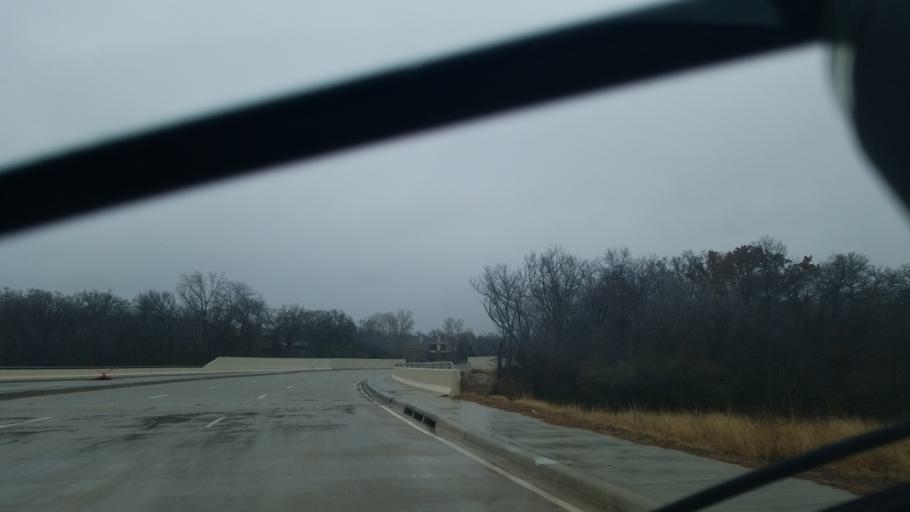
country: US
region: Texas
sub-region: Denton County
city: Corinth
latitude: 33.1364
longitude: -97.0952
